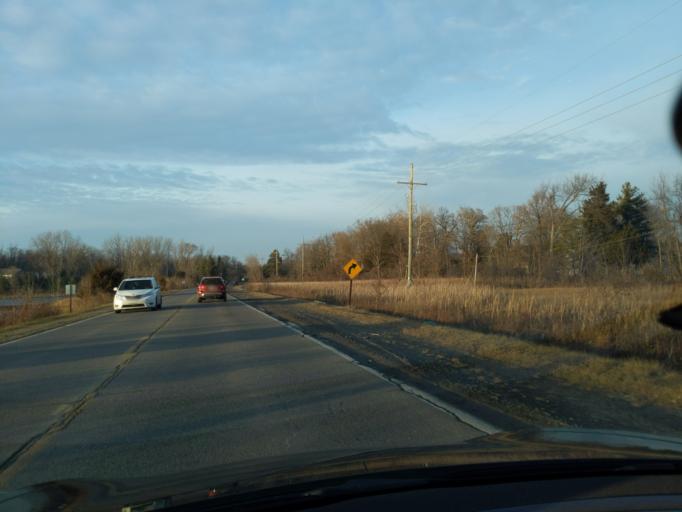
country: US
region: Michigan
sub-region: Livingston County
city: Brighton
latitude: 42.5567
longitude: -83.7544
